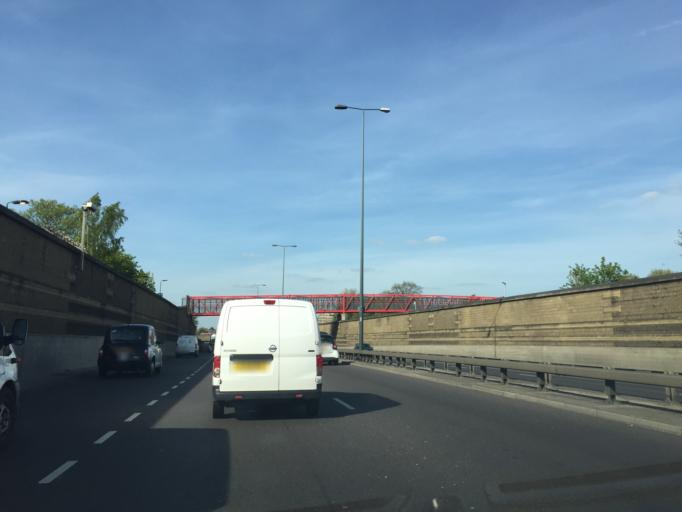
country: GB
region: England
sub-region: Greater London
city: Walthamstow
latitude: 51.5658
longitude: 0.0059
